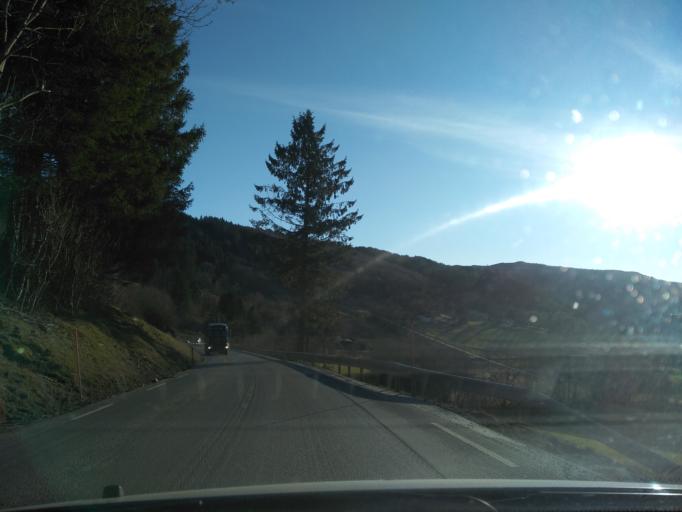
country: NO
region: Rogaland
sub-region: Vindafjord
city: Olen
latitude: 59.6142
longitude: 5.8750
